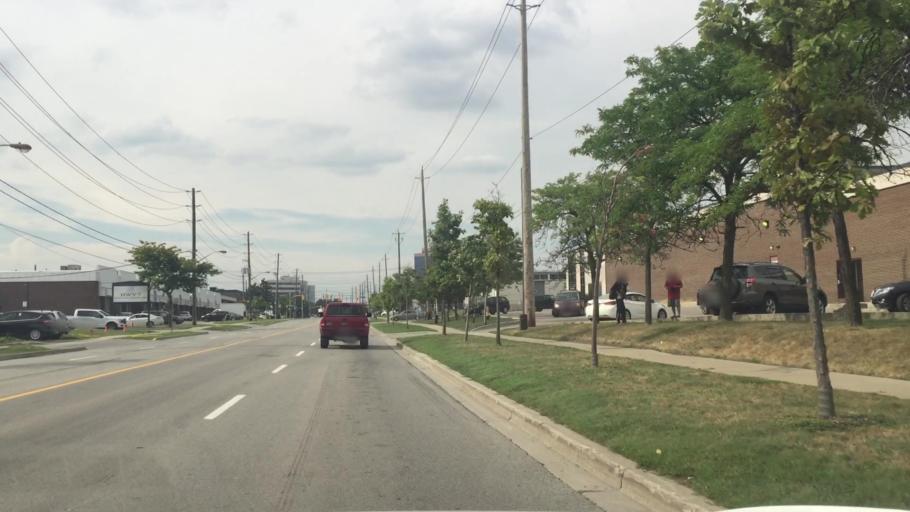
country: CA
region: Ontario
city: Concord
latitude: 43.7663
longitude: -79.5413
